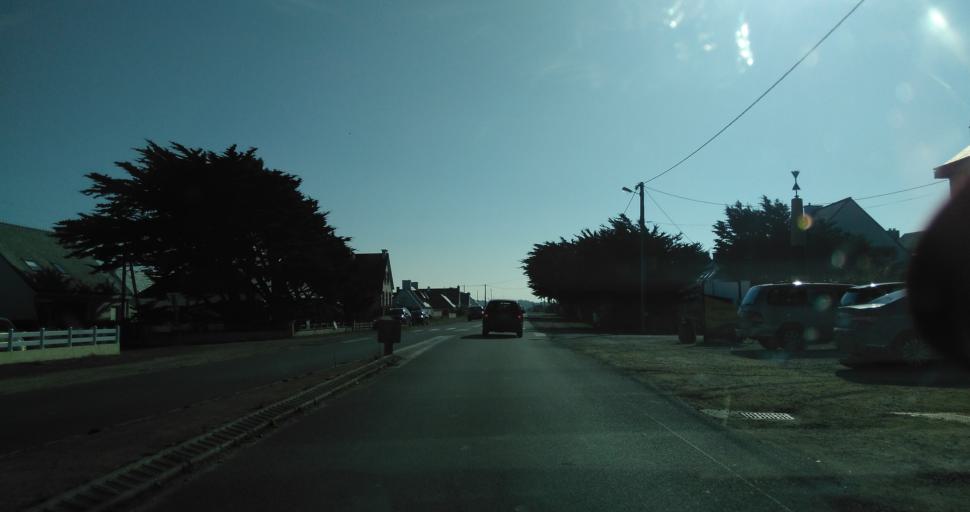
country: FR
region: Brittany
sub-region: Departement du Morbihan
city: Saint-Pierre-Quiberon
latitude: 47.5539
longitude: -3.1342
